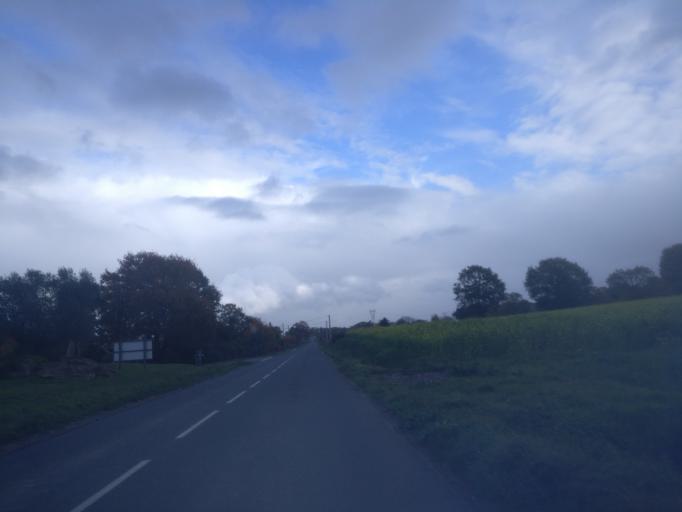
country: FR
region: Brittany
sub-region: Departement d'Ille-et-Vilaine
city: Goven
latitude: 48.0349
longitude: -1.8201
